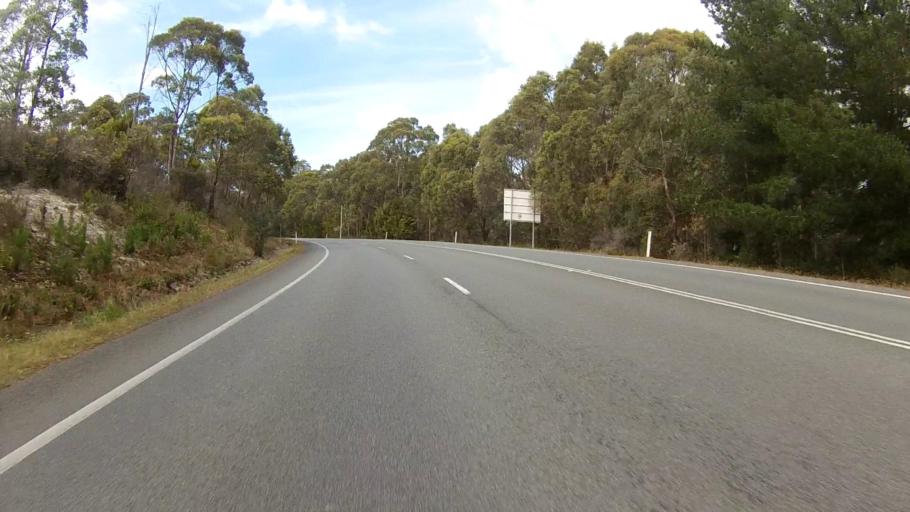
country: AU
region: Tasmania
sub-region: Kingborough
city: Kettering
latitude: -43.1087
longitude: 147.2426
